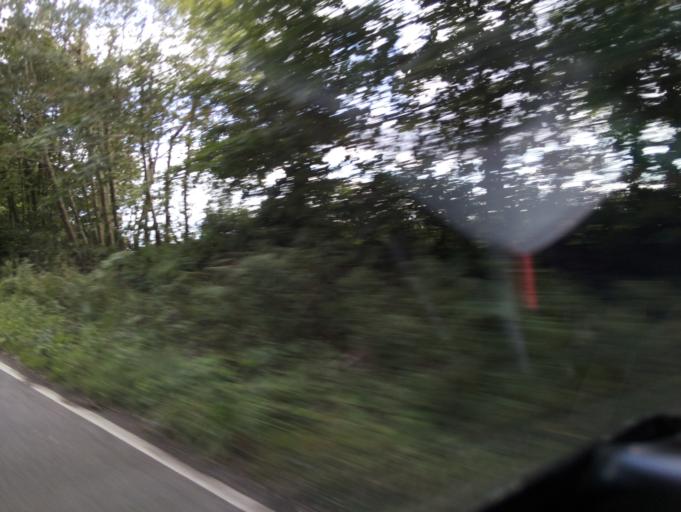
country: GB
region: England
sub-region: Devon
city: Honiton
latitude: 50.7496
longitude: -3.2086
